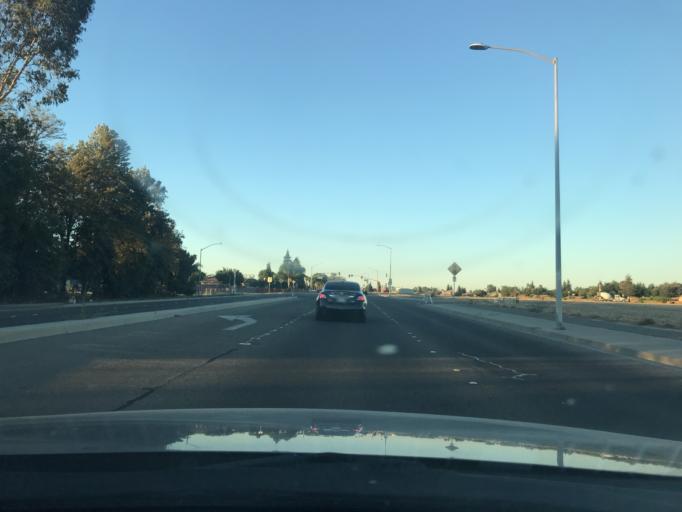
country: US
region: California
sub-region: Merced County
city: Atwater
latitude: 37.3517
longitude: -120.5768
